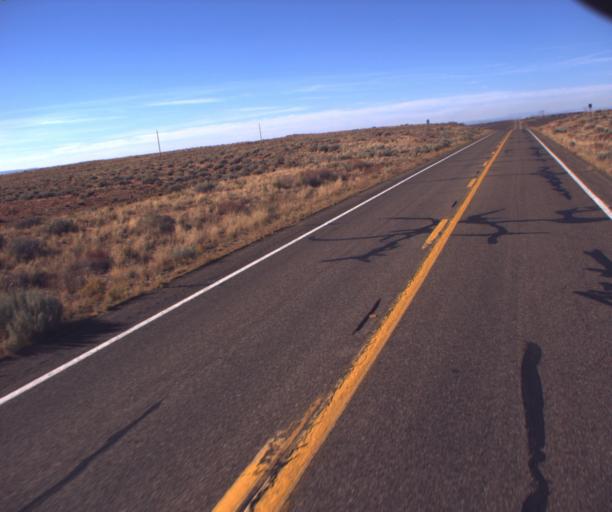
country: US
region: Arizona
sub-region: Coconino County
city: LeChee
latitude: 36.7771
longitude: -111.2876
